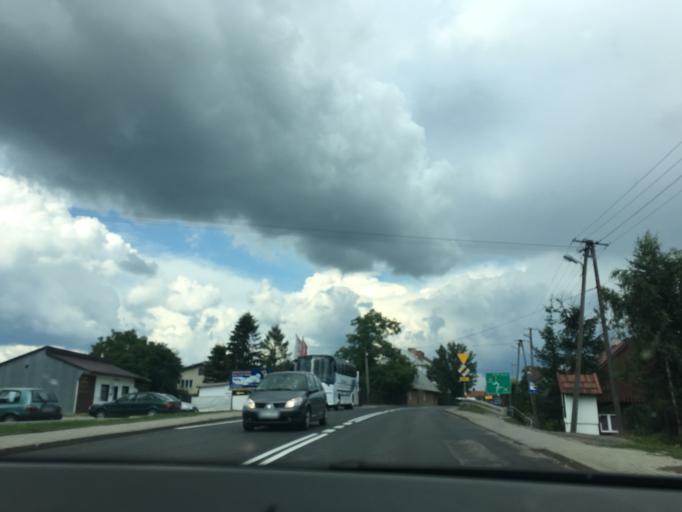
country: PL
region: Subcarpathian Voivodeship
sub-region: Powiat krosnienski
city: Miejsce Piastowe
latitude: 49.6336
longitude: 21.7852
